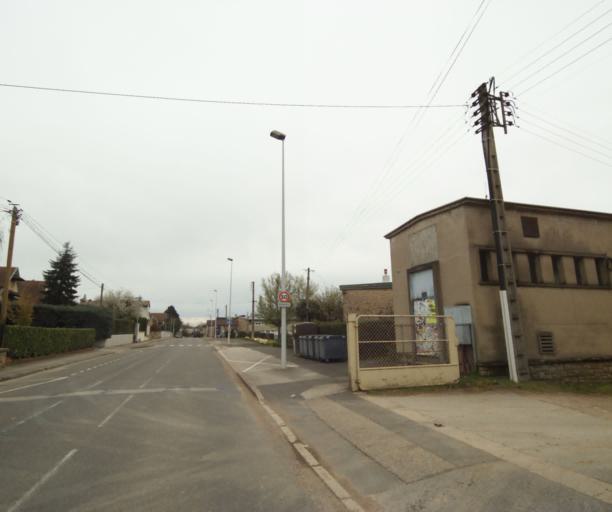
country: FR
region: Bourgogne
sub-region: Departement de Saone-et-Loire
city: Macon
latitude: 46.3014
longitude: 4.8114
